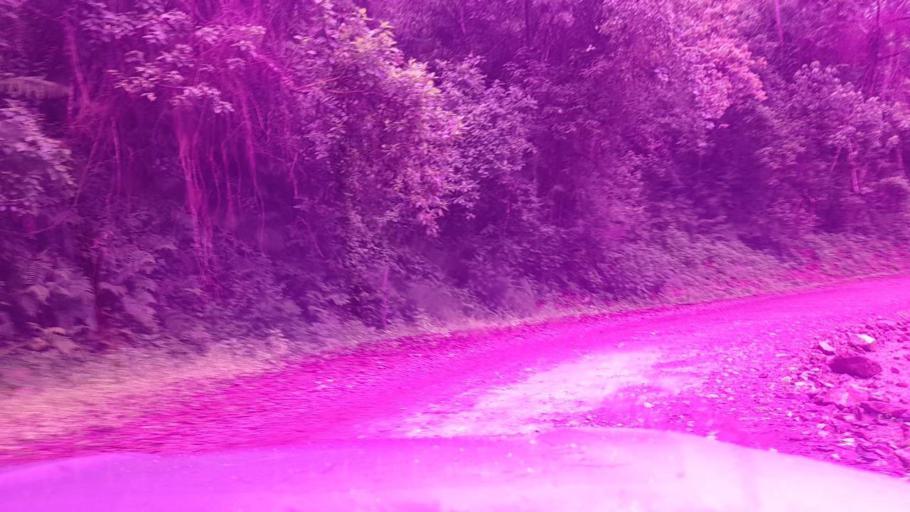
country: ET
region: Southern Nations, Nationalities, and People's Region
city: Bonga
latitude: 7.5117
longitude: 36.0573
